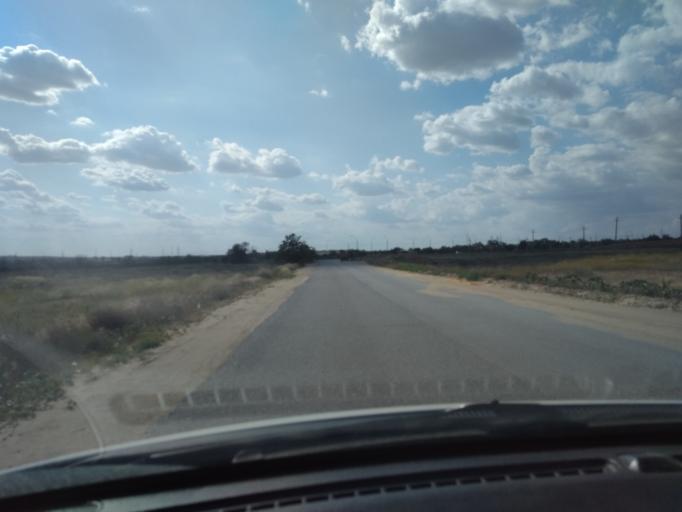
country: RU
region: Volgograd
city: Vodstroy
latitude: 48.8062
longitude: 44.5265
